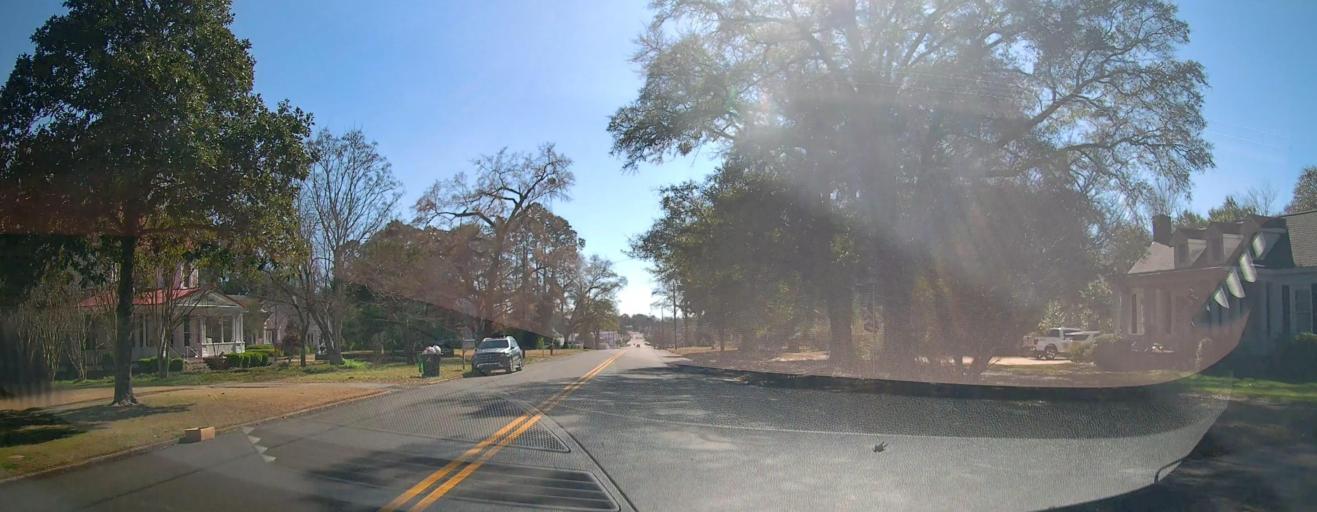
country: US
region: Georgia
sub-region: Macon County
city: Montezuma
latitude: 32.3048
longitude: -84.0280
